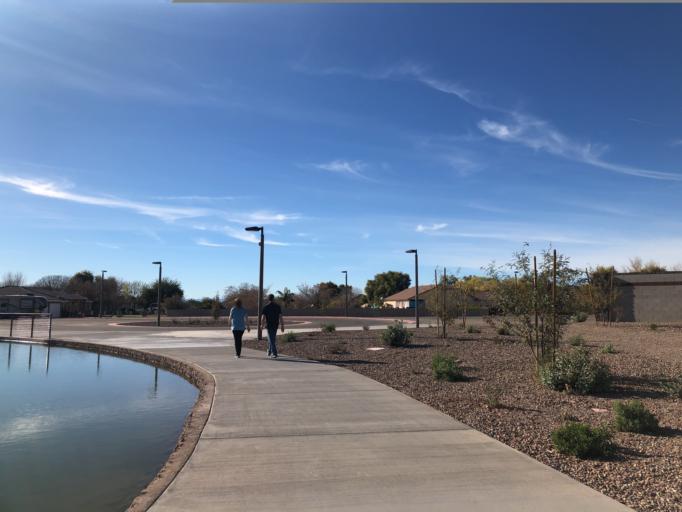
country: US
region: Arizona
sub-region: Maricopa County
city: Queen Creek
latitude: 33.2571
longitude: -111.6597
